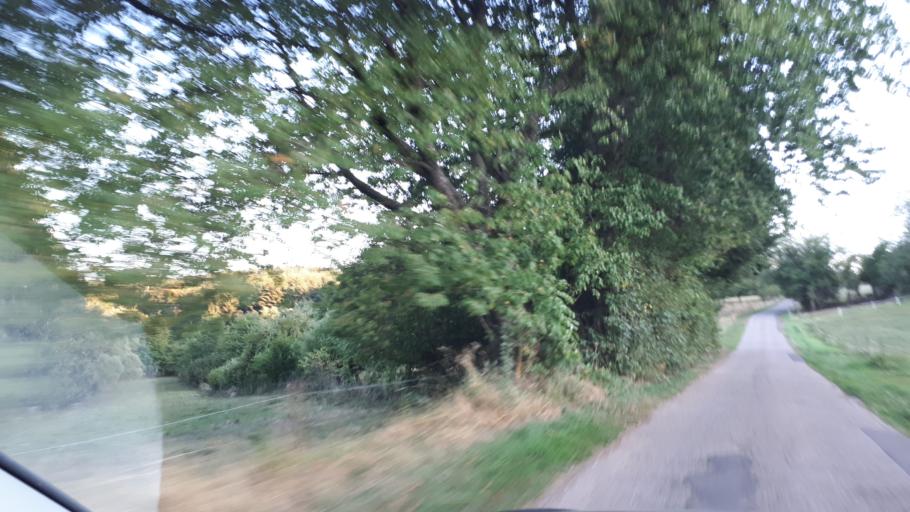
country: DE
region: Saarland
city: Eppelborn
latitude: 49.3969
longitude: 7.0054
